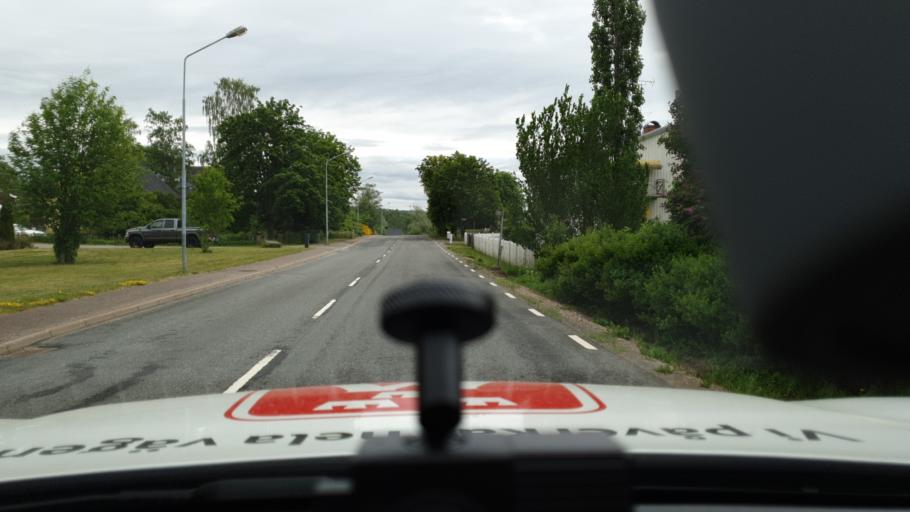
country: SE
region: Joenkoeping
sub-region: Mullsjo Kommun
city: Mullsjoe
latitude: 57.9889
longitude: 13.7584
